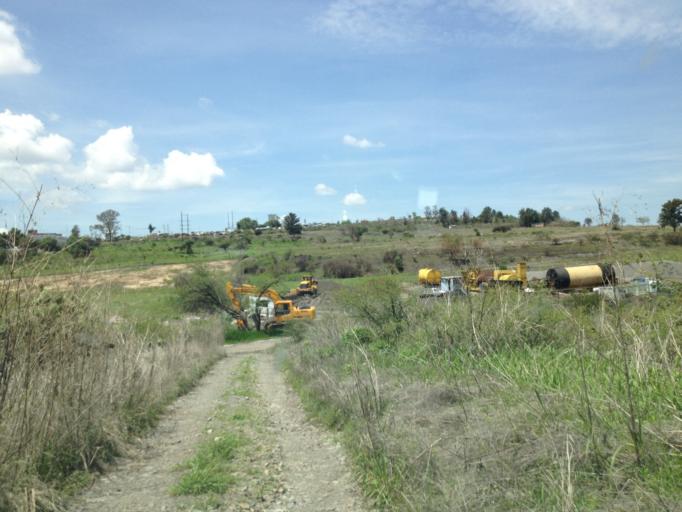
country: MX
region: Michoacan
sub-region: Tarimbaro
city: San Bernabe de las Canteras
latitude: 19.7648
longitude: -101.1667
